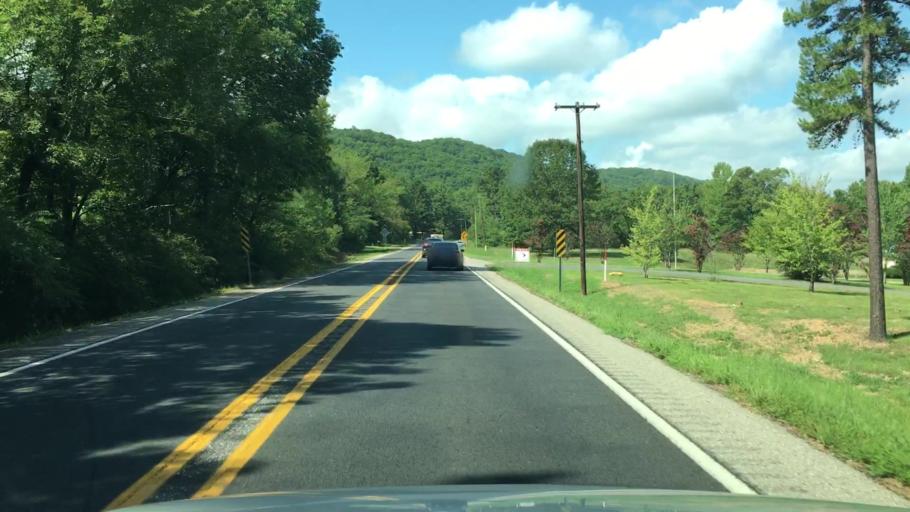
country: US
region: Arkansas
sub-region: Garland County
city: Lake Hamilton
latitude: 34.3808
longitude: -93.1355
